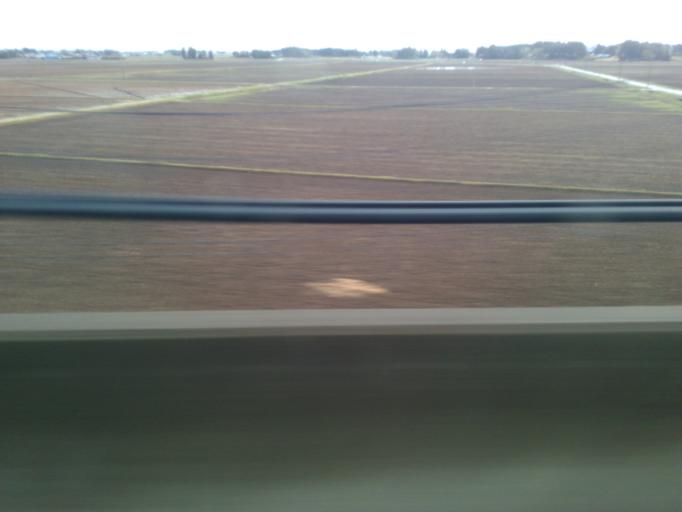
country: JP
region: Miyagi
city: Furukawa
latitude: 38.5469
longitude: 140.9618
